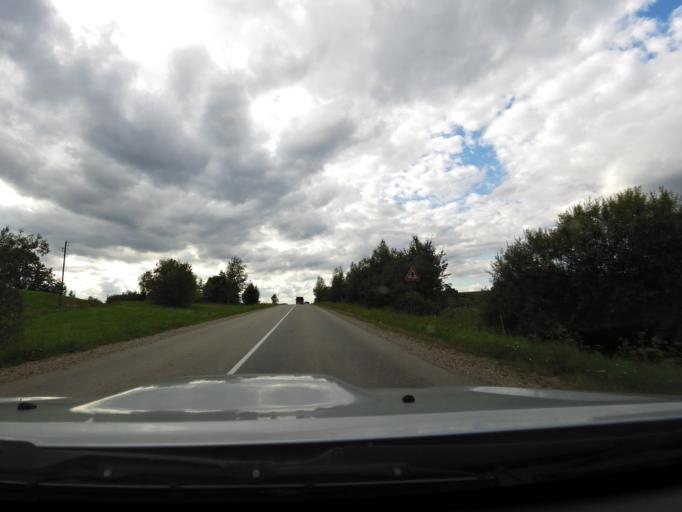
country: LV
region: Ilukste
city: Ilukste
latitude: 55.9793
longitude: 26.0072
